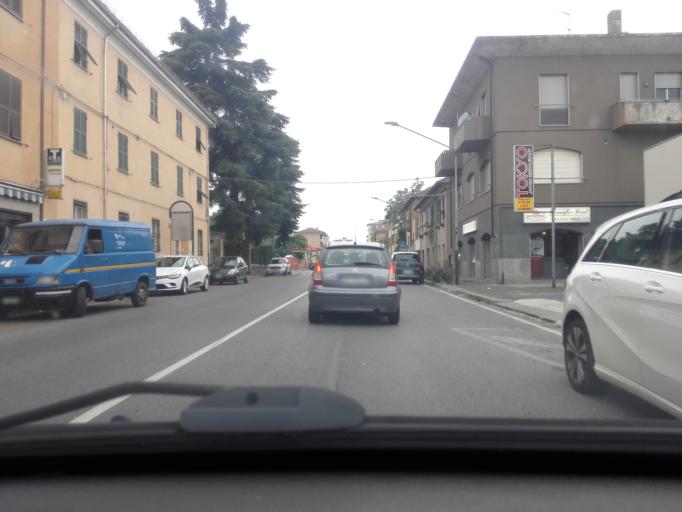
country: IT
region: Piedmont
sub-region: Provincia di Alessandria
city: Novi Ligure
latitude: 44.7706
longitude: 8.7891
